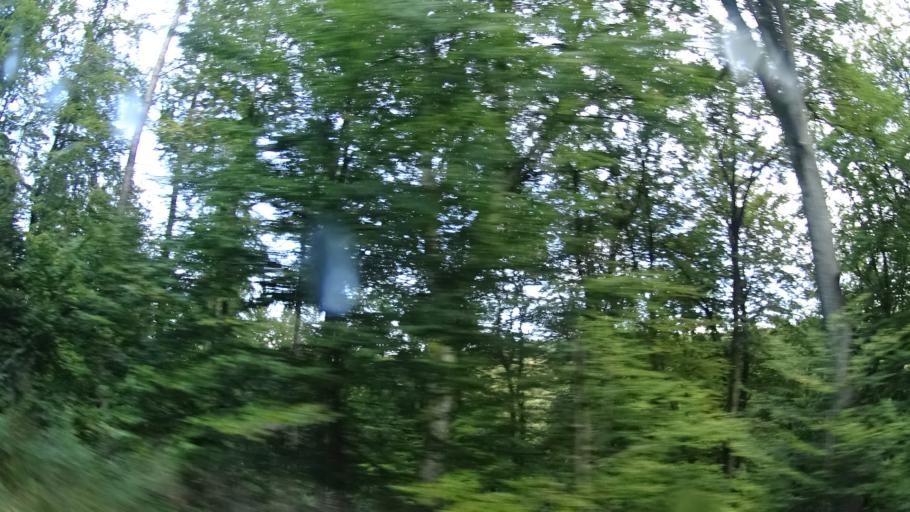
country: DE
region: Baden-Wuerttemberg
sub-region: Karlsruhe Region
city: Hopfingen
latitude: 49.6271
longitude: 9.4415
